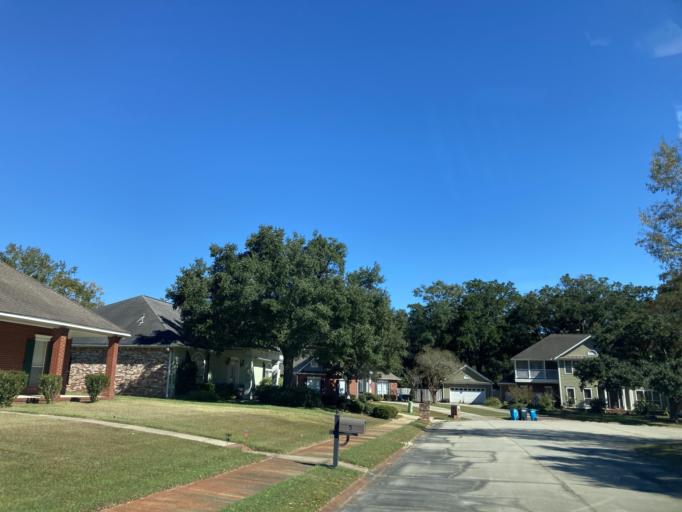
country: US
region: Mississippi
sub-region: Jackson County
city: Ocean Springs
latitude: 30.4025
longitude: -88.8113
